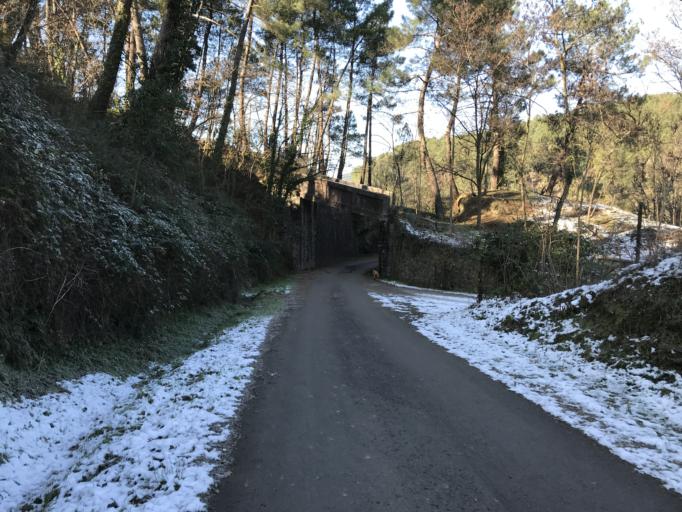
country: FR
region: Languedoc-Roussillon
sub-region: Departement du Gard
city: Saint-Florent-sur-Auzonnet
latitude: 44.2340
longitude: 4.1352
